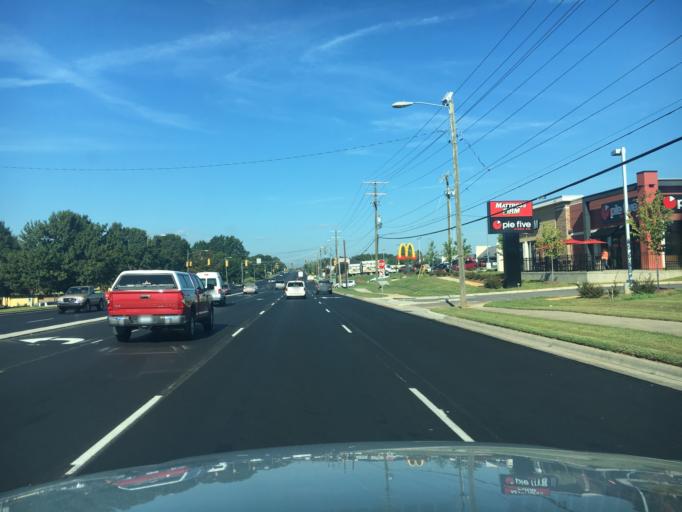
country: US
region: North Carolina
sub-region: Catawba County
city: Hickory
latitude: 35.7044
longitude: -81.2995
